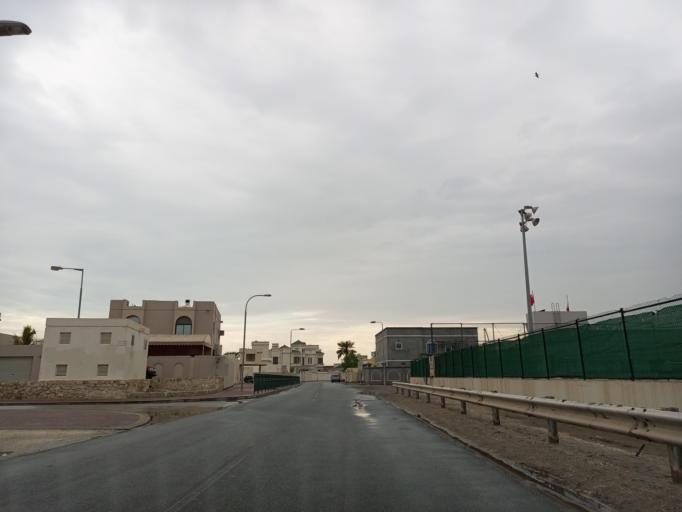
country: BH
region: Muharraq
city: Al Hadd
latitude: 26.2418
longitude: 50.6350
